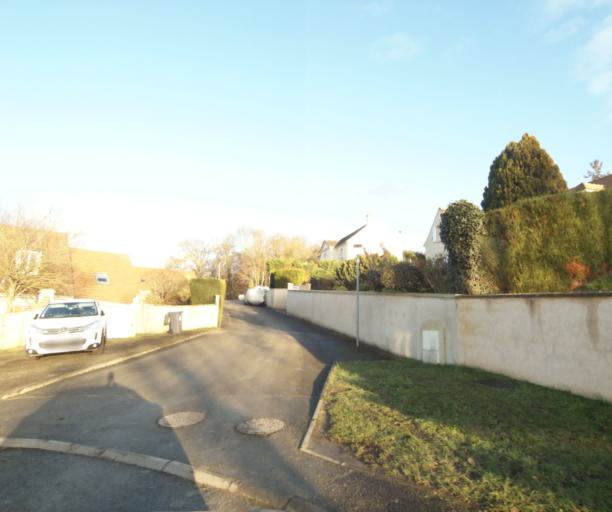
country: FR
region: Ile-de-France
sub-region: Departement des Yvelines
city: Meulan-en-Yvelines
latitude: 49.0146
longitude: 1.9188
